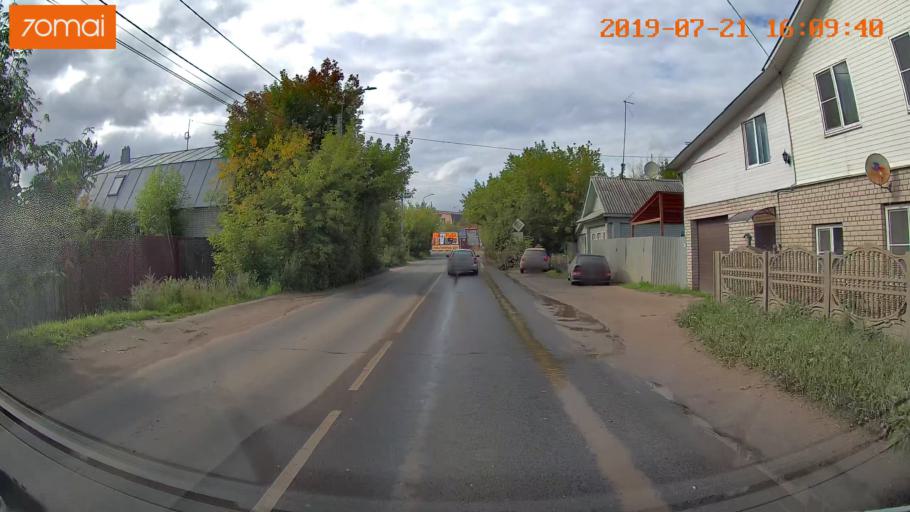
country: RU
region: Ivanovo
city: Bogorodskoye
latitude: 57.0060
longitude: 41.0270
